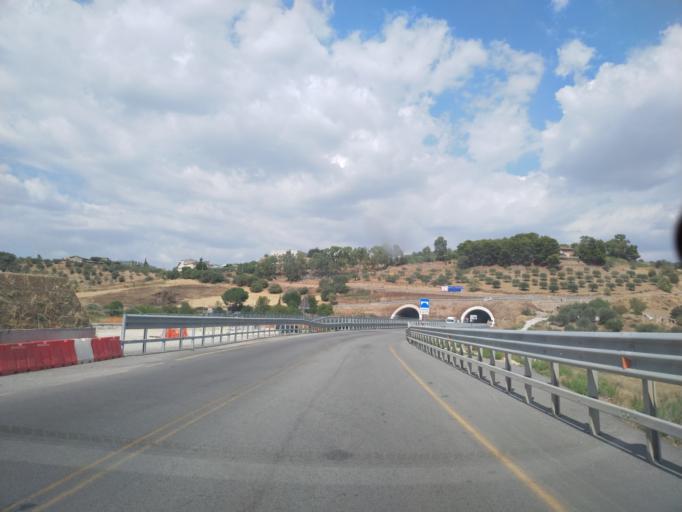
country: IT
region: Sicily
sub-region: Provincia di Caltanissetta
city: San Cataldo
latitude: 37.4579
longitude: 13.9938
